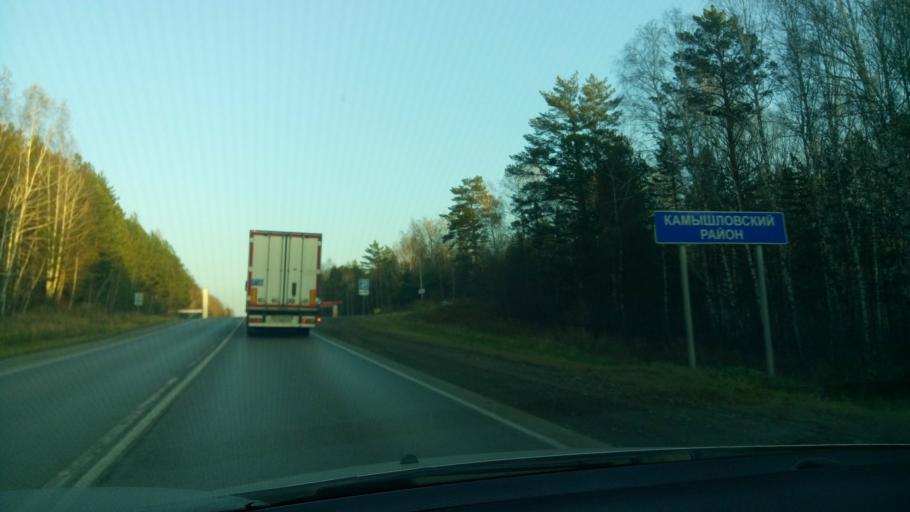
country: RU
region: Sverdlovsk
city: Yelanskiy
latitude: 56.7581
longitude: 62.3242
